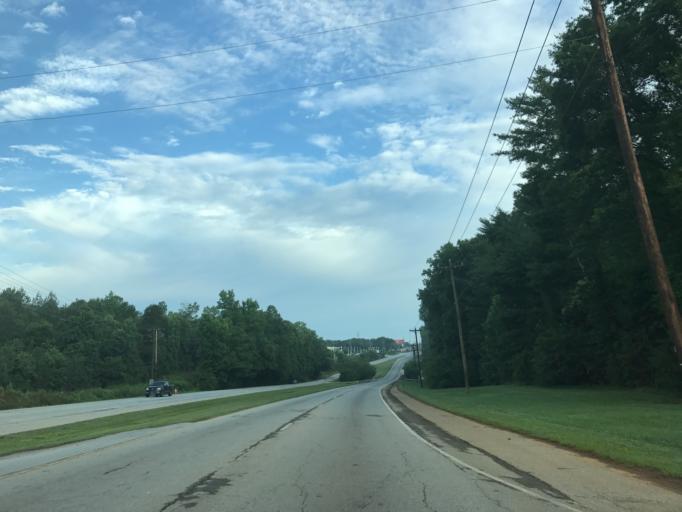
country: US
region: South Carolina
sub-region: Greenville County
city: Mauldin
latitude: 34.8050
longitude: -82.3249
